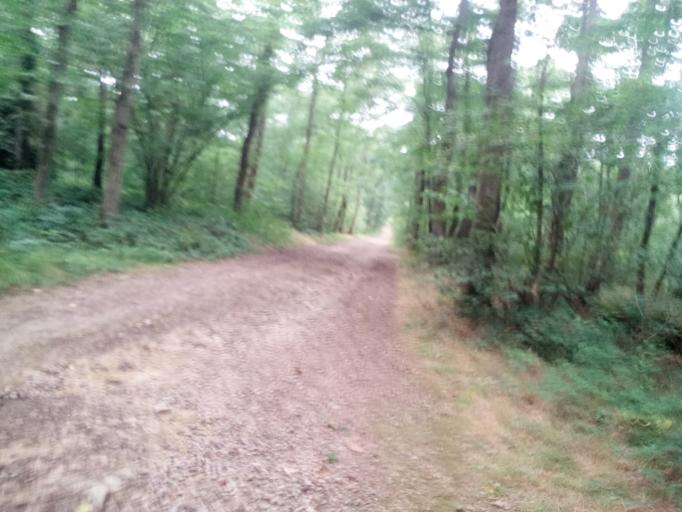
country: FR
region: Lower Normandy
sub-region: Departement du Calvados
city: Clinchamps-sur-Orne
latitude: 49.0459
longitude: -0.4317
